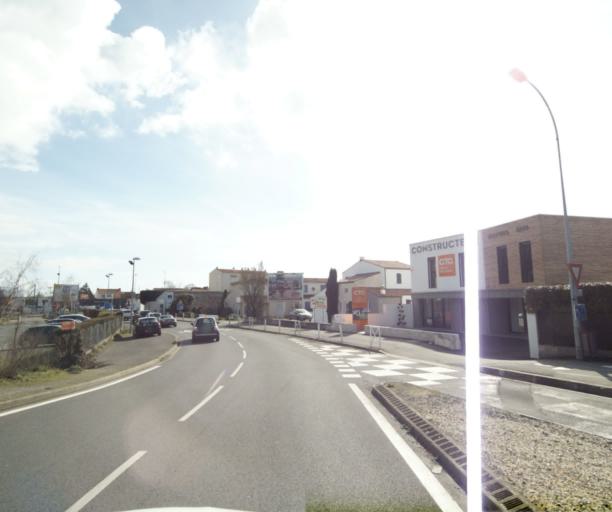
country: FR
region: Poitou-Charentes
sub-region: Departement de la Charente-Maritime
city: Lagord
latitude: 46.1779
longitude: -1.1527
